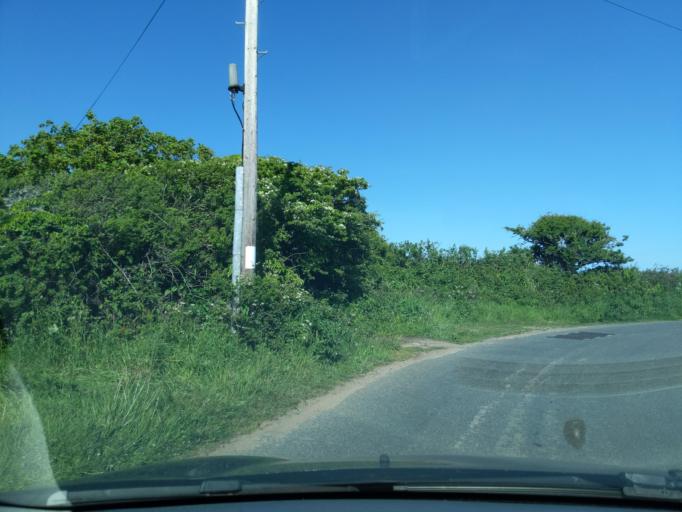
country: GB
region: England
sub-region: Cornwall
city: St. Buryan
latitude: 50.0734
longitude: -5.6149
